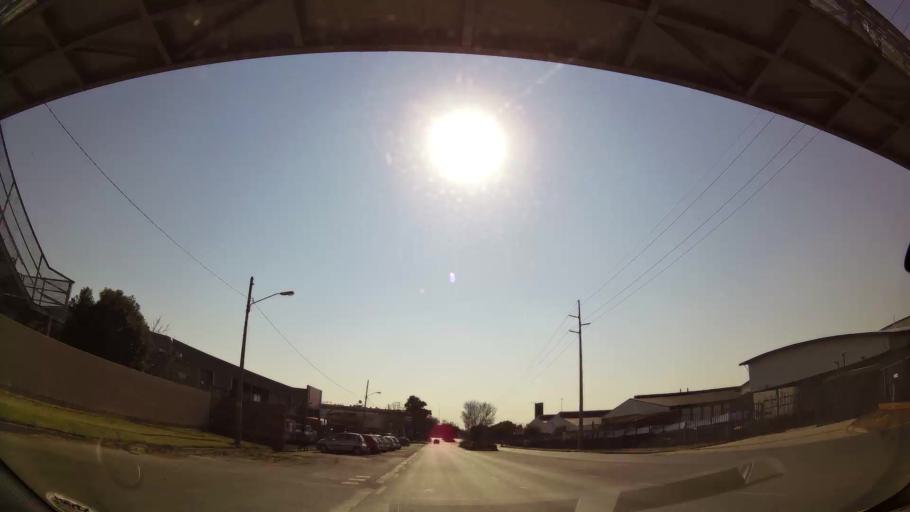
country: ZA
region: Gauteng
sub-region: City of Johannesburg Metropolitan Municipality
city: Modderfontein
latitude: -26.1331
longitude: 28.2164
